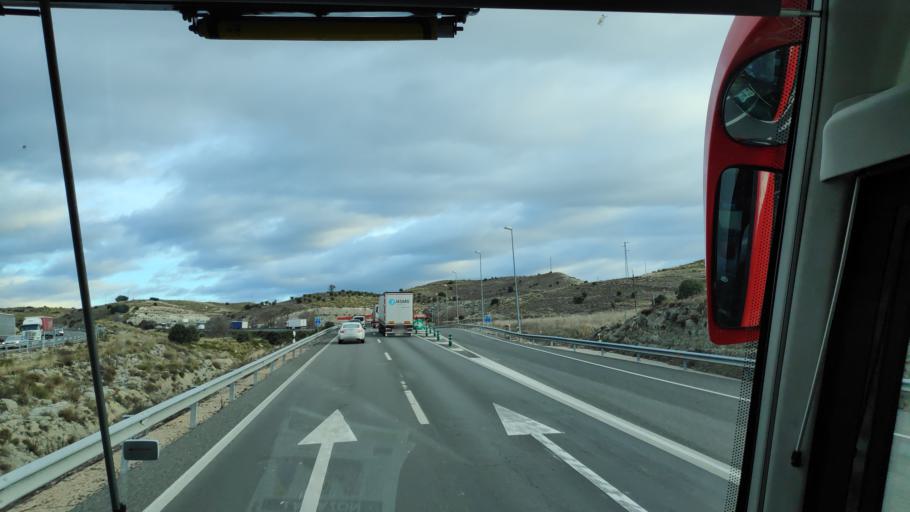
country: ES
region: Madrid
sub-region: Provincia de Madrid
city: Perales de Tajuna
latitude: 40.2093
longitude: -3.3220
